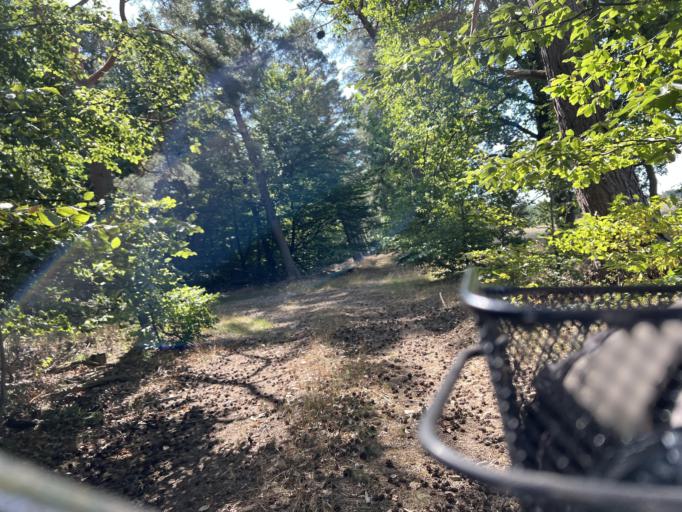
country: DE
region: Lower Saxony
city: Tosterglope
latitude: 53.1972
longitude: 10.8088
